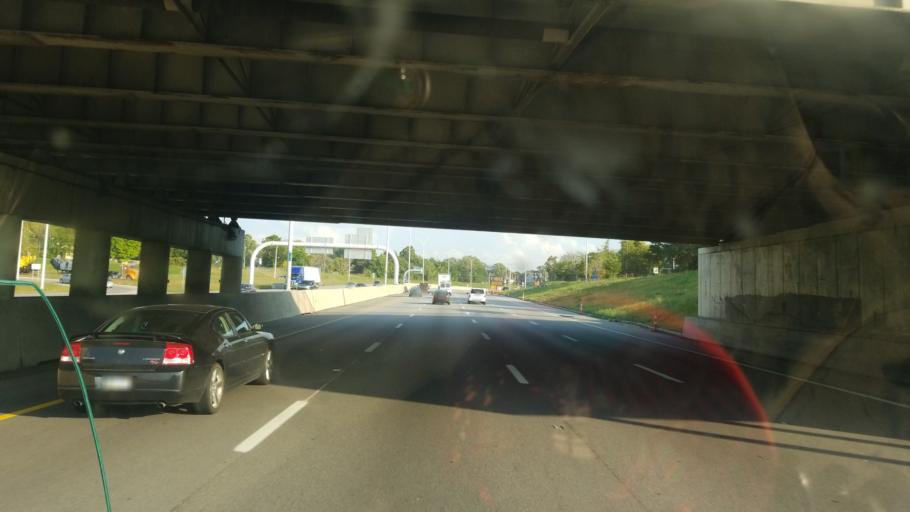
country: US
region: Ohio
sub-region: Lucas County
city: Toledo
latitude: 41.6672
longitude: -83.5688
